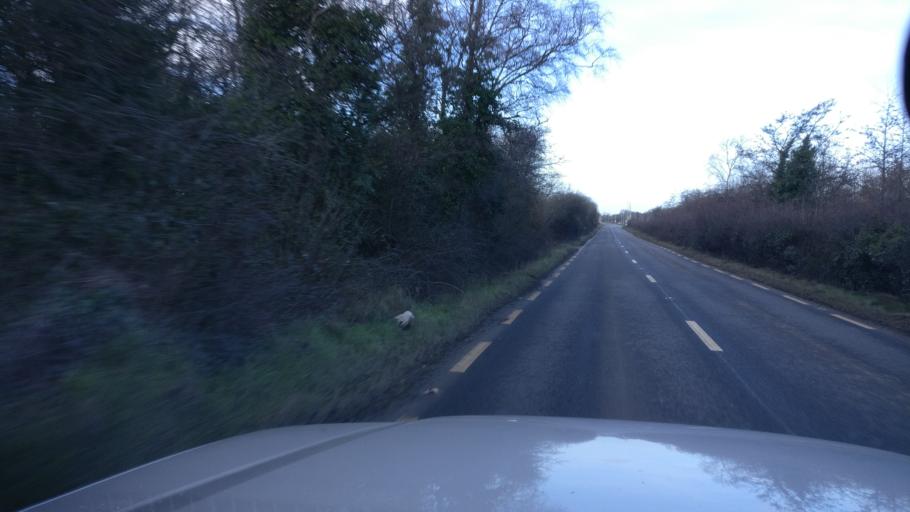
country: IE
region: Leinster
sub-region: Laois
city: Portlaoise
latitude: 53.0625
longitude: -7.3252
